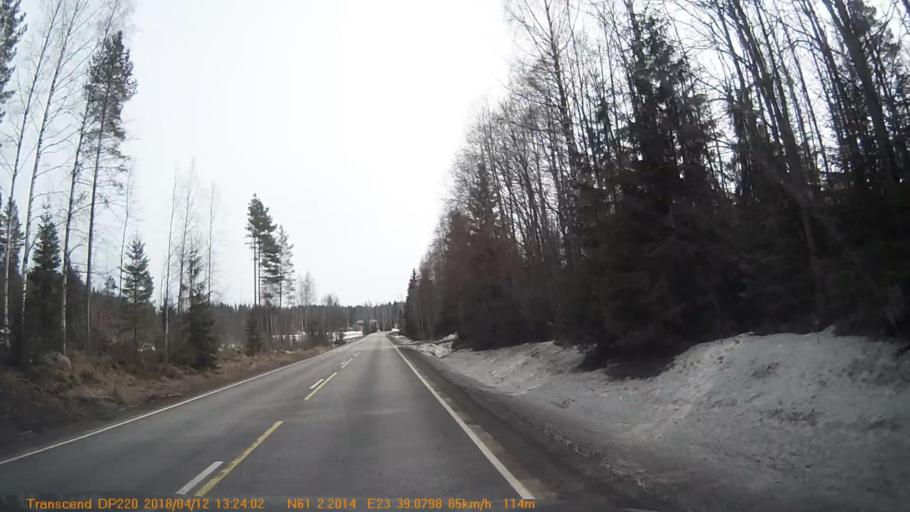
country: FI
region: Pirkanmaa
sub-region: Etelae-Pirkanmaa
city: Kylmaekoski
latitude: 61.0357
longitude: 23.6529
